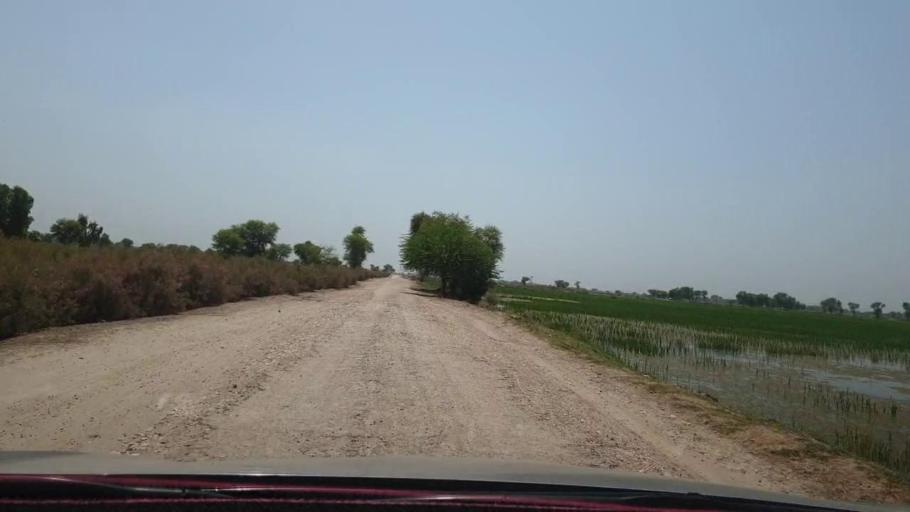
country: PK
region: Sindh
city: Kambar
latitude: 27.5697
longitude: 67.8808
